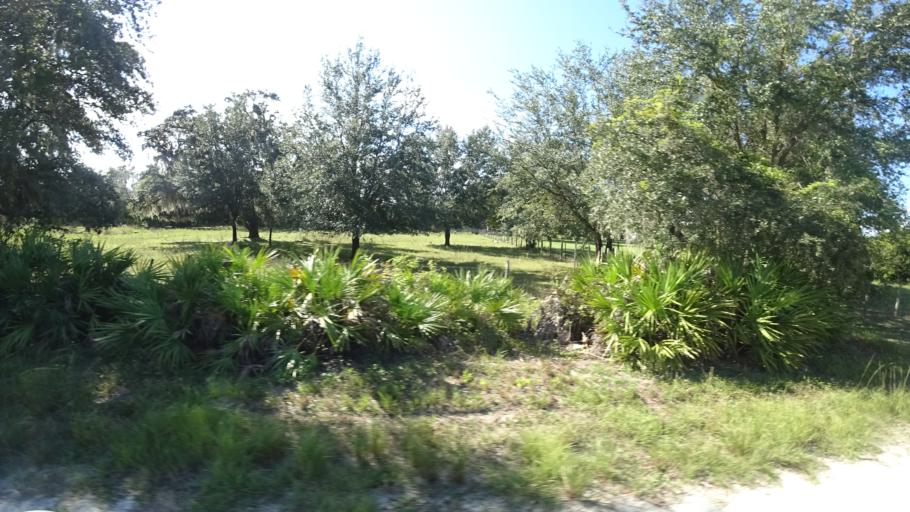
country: US
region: Florida
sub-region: Hardee County
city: Wauchula
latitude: 27.4739
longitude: -82.0555
